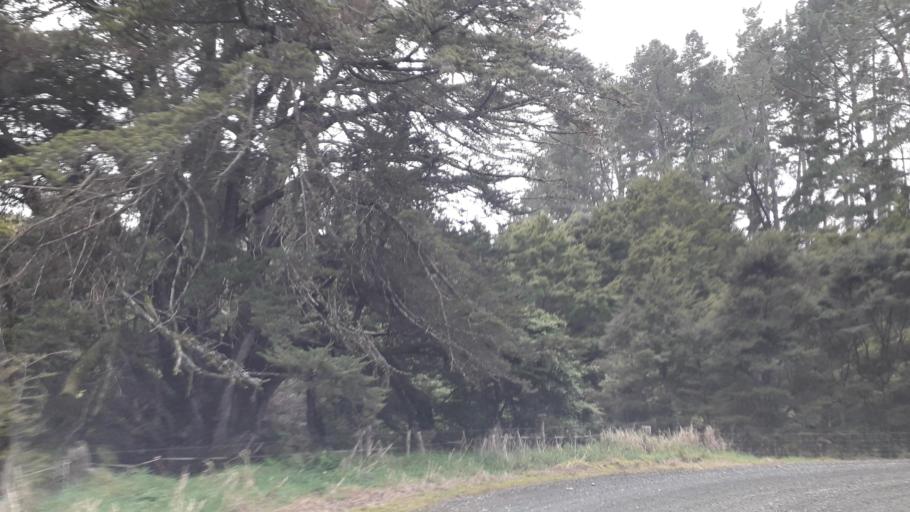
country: NZ
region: Northland
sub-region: Far North District
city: Waimate North
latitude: -35.1334
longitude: 173.7157
